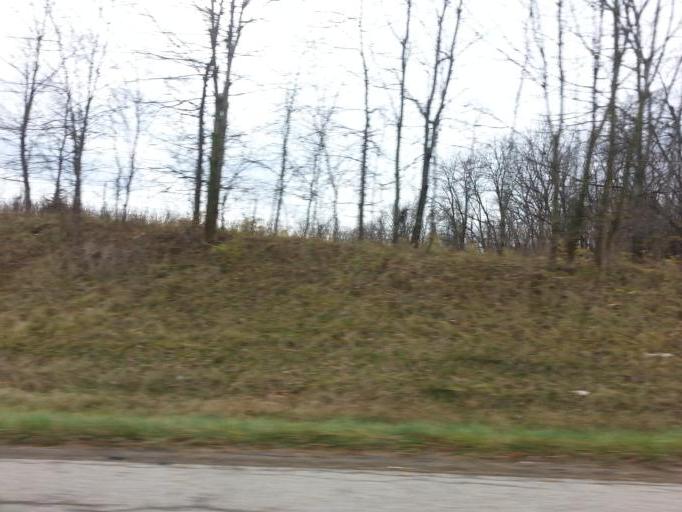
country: US
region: Indiana
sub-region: Decatur County
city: Greensburg
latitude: 39.3366
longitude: -85.4048
